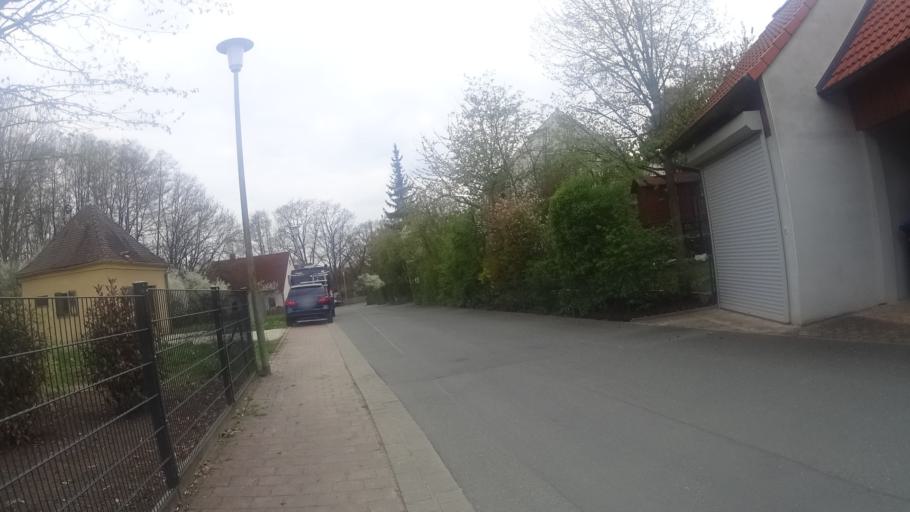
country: DE
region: Bavaria
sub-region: Upper Franconia
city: Igensdorf
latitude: 49.6047
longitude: 11.2037
